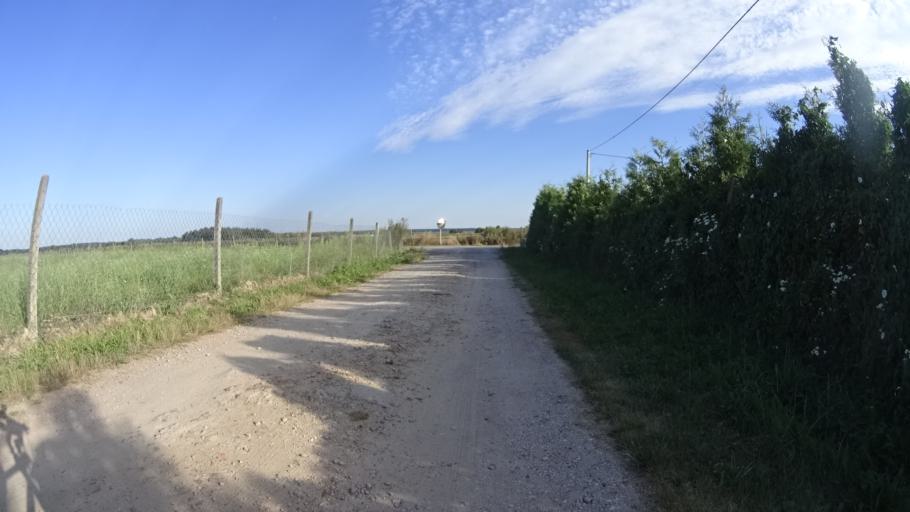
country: PL
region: Masovian Voivodeship
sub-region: Powiat bialobrzeski
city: Wysmierzyce
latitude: 51.6774
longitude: 20.8183
